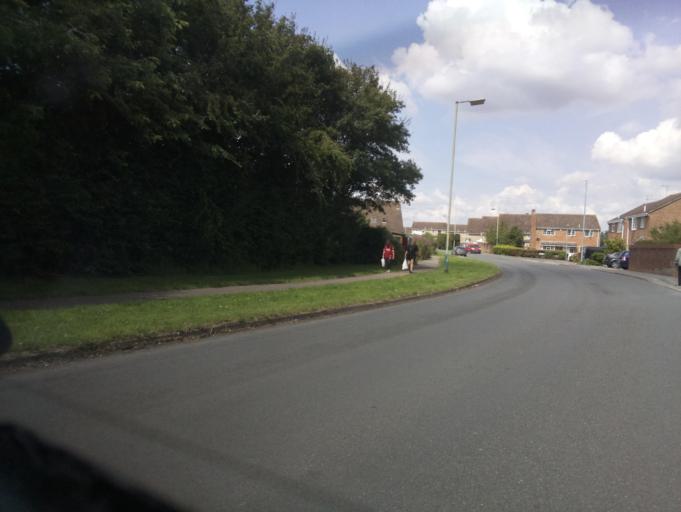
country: GB
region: England
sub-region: Wiltshire
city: Lydiard Tregoze
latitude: 51.5530
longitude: -1.8340
